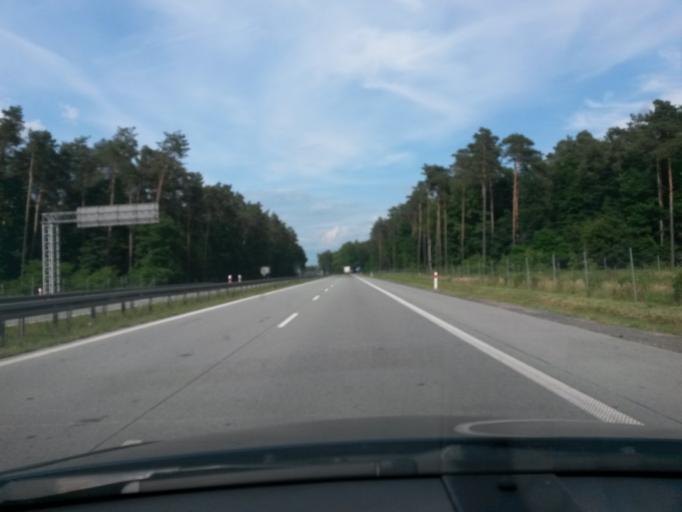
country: PL
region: Lodz Voivodeship
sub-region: Powiat skierniewicki
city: Kowiesy
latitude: 51.9293
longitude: 20.4684
